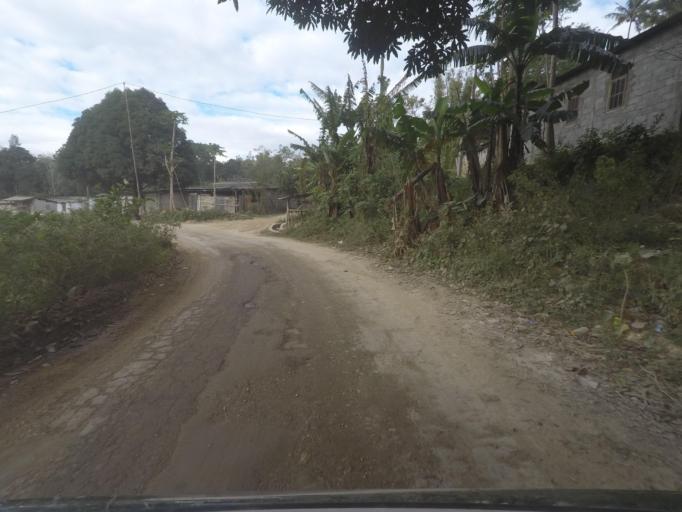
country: TL
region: Baucau
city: Venilale
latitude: -8.6091
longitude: 126.3821
